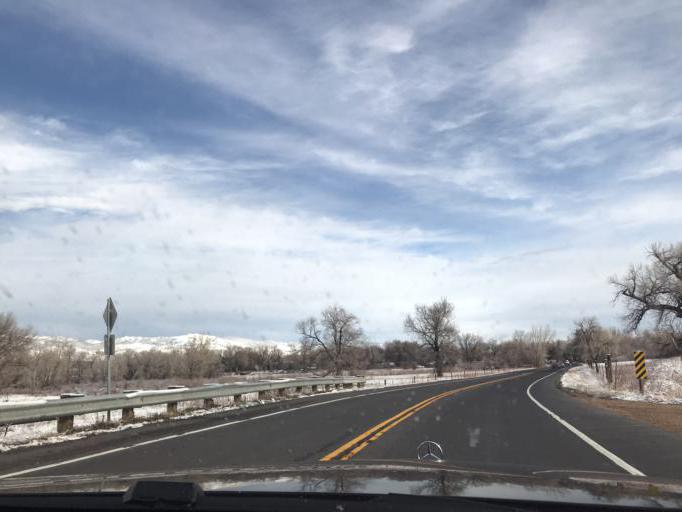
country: US
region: Colorado
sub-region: Boulder County
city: Boulder
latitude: 39.9965
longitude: -105.2127
